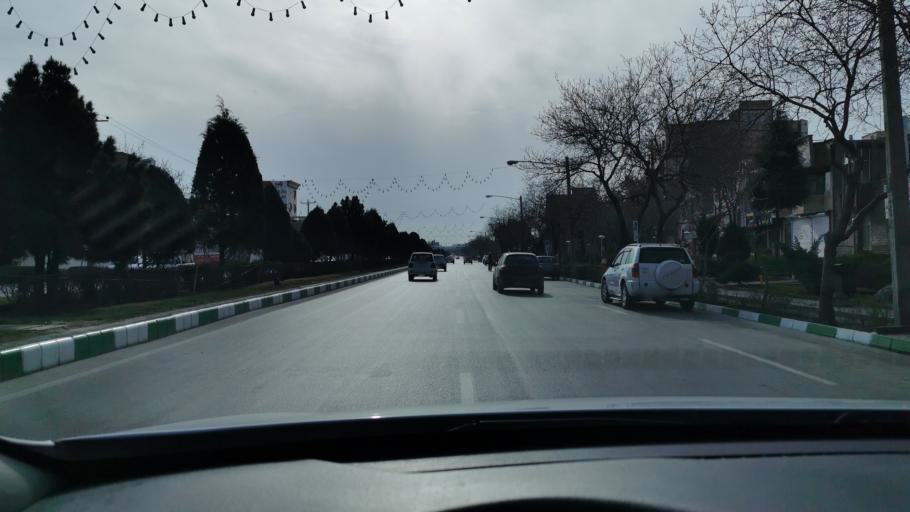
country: IR
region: Razavi Khorasan
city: Mashhad
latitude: 36.3041
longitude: 59.5138
